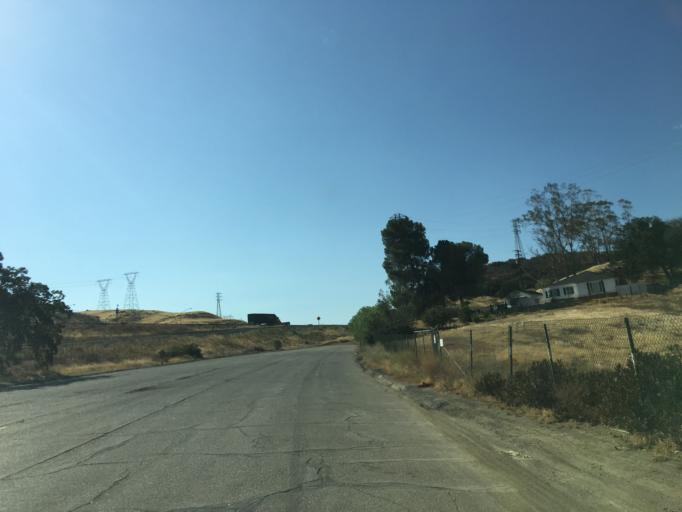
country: US
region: California
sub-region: Los Angeles County
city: Castaic
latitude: 34.5686
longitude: -118.6886
